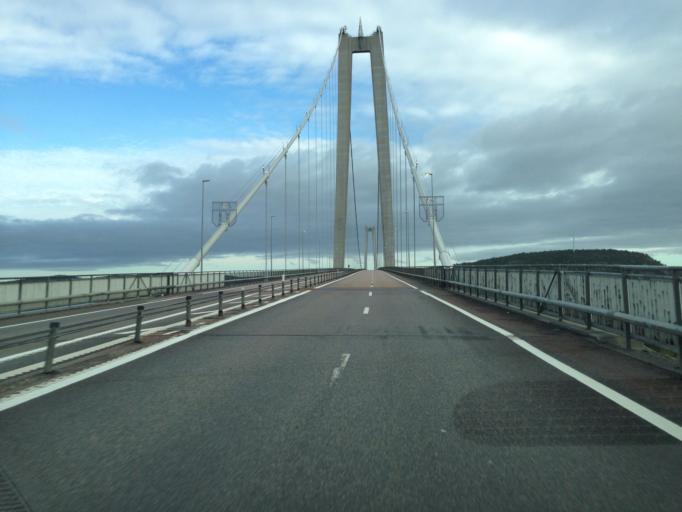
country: SE
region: Vaesternorrland
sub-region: Haernoesands Kommun
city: Haernoesand
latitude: 62.7911
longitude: 17.9273
